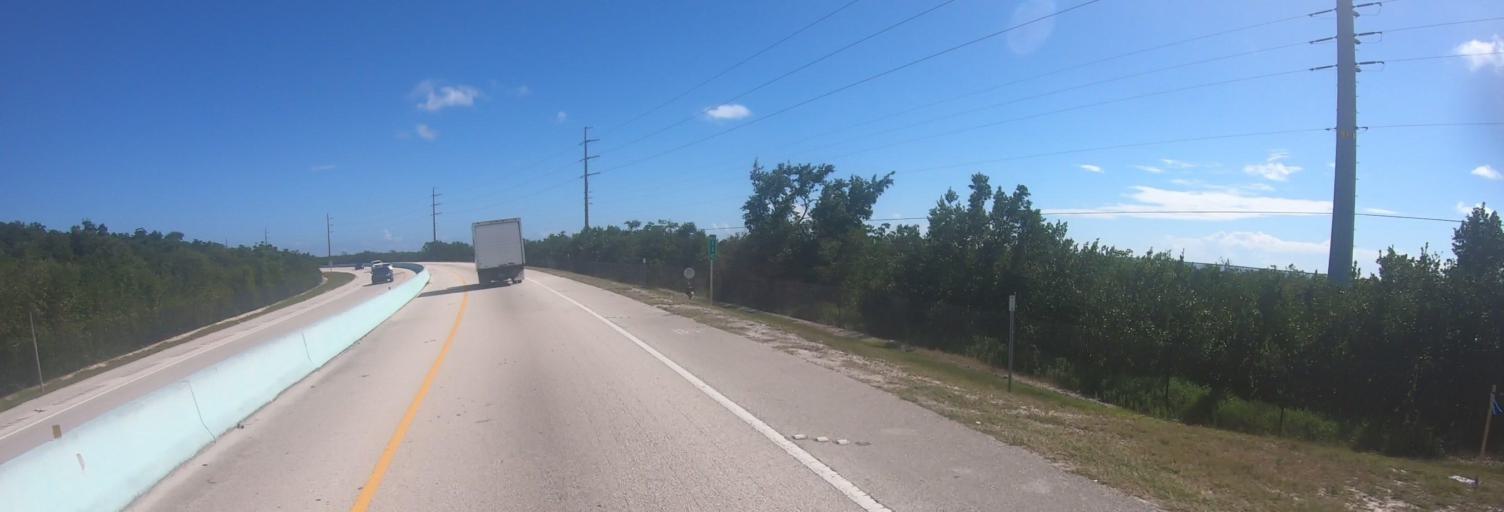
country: US
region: Florida
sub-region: Monroe County
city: Key Largo
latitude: 25.1980
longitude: -80.4171
